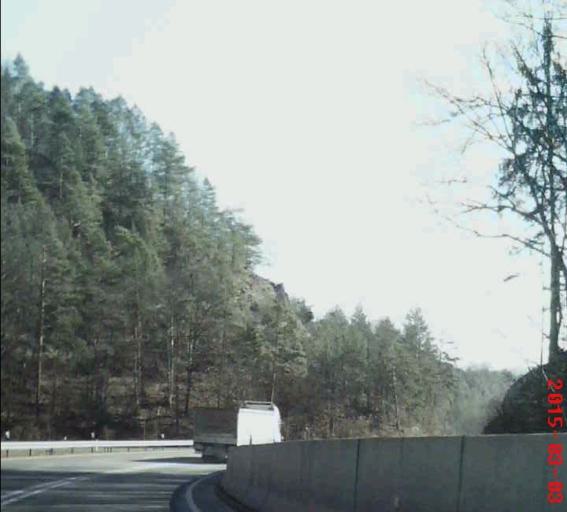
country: DE
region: Thuringia
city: Bad Blankenburg
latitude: 50.7270
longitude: 11.2540
